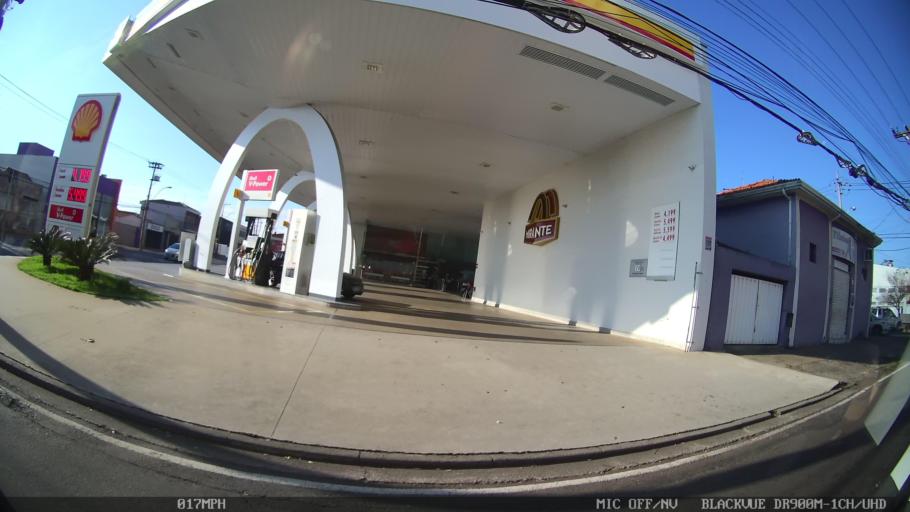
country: BR
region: Sao Paulo
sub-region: Piracicaba
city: Piracicaba
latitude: -22.7123
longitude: -47.6560
